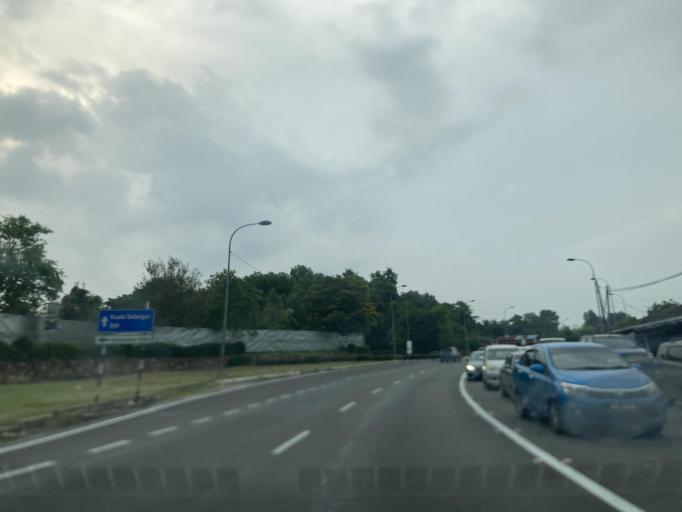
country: MY
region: Selangor
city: Kuang
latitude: 3.2162
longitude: 101.5300
